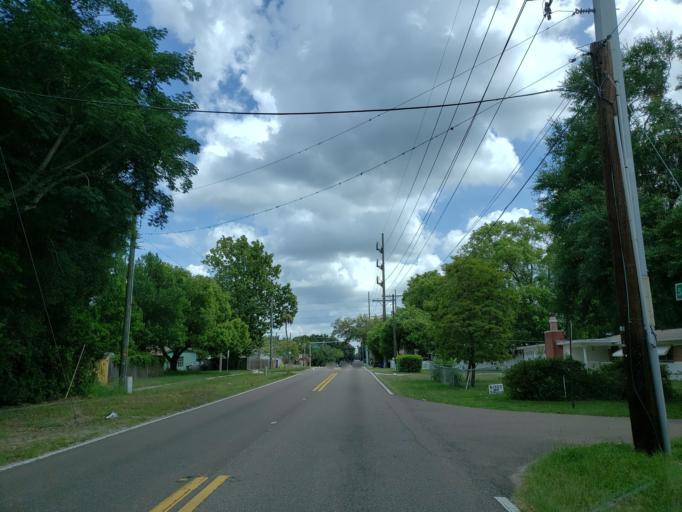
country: US
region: Florida
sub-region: Hillsborough County
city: Seffner
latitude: 27.9729
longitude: -82.2777
